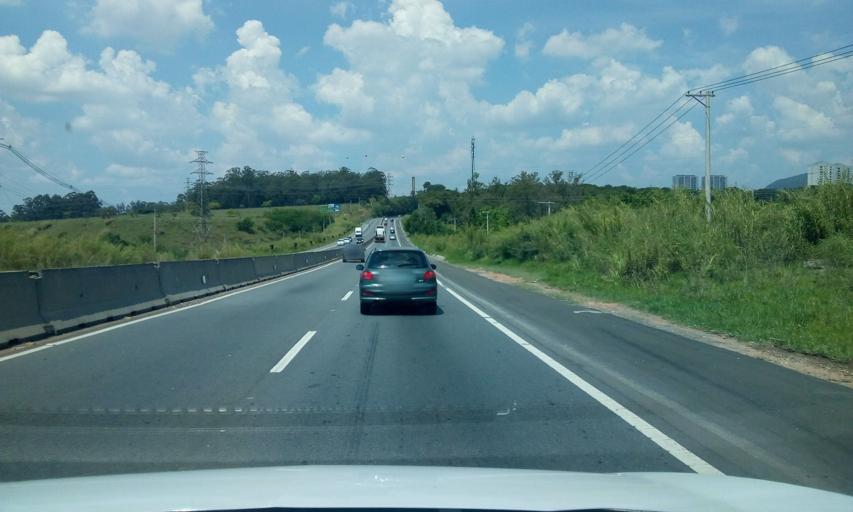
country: BR
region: Sao Paulo
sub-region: Itupeva
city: Itupeva
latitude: -23.1780
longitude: -46.9780
